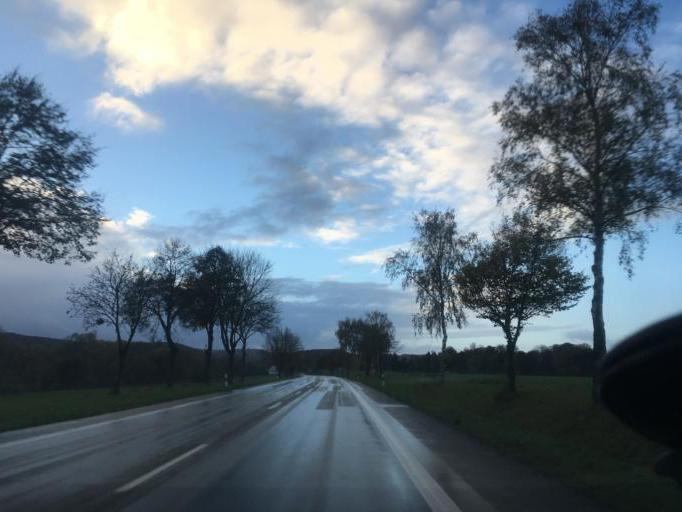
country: DE
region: Lower Saxony
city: Hardegsen
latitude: 51.6399
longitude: 9.8799
